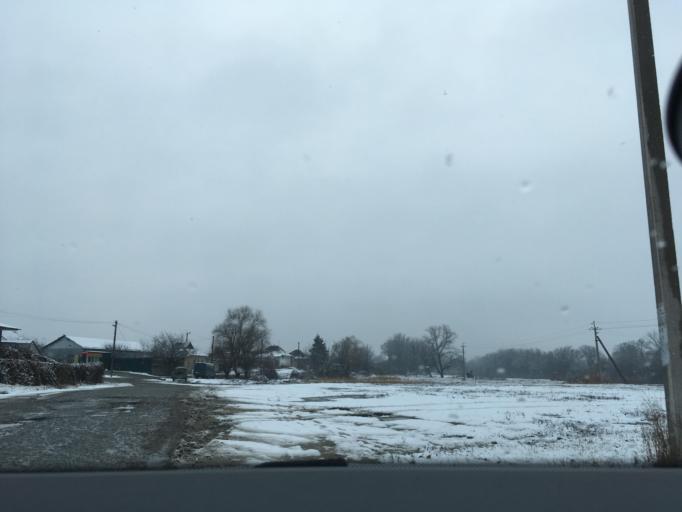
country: RU
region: Belgorod
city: Valuyki
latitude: 50.2056
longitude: 38.1033
